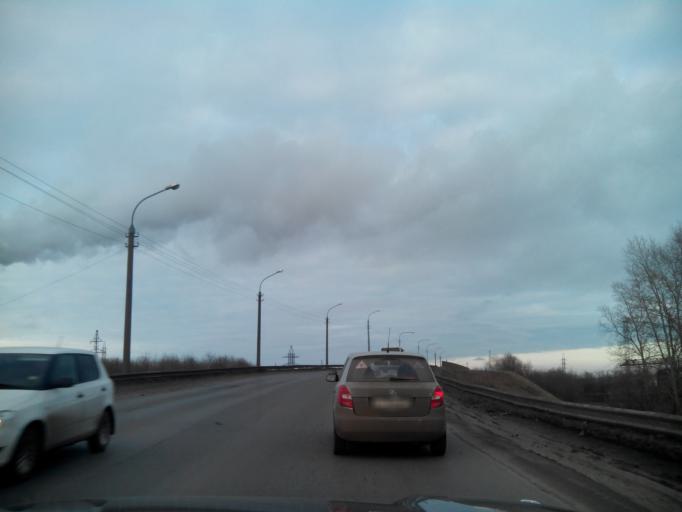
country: RU
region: Arkhangelskaya
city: Arkhangel'sk
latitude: 64.5663
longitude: 40.5561
